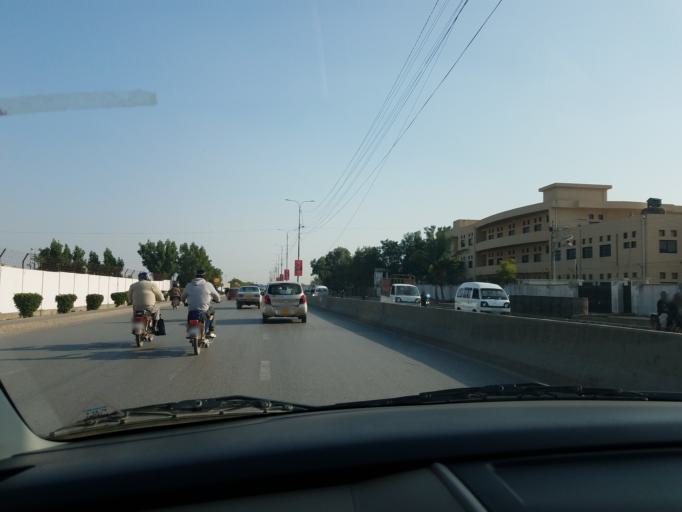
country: PK
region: Sindh
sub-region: Karachi District
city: Karachi
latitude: 24.8948
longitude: 67.1199
